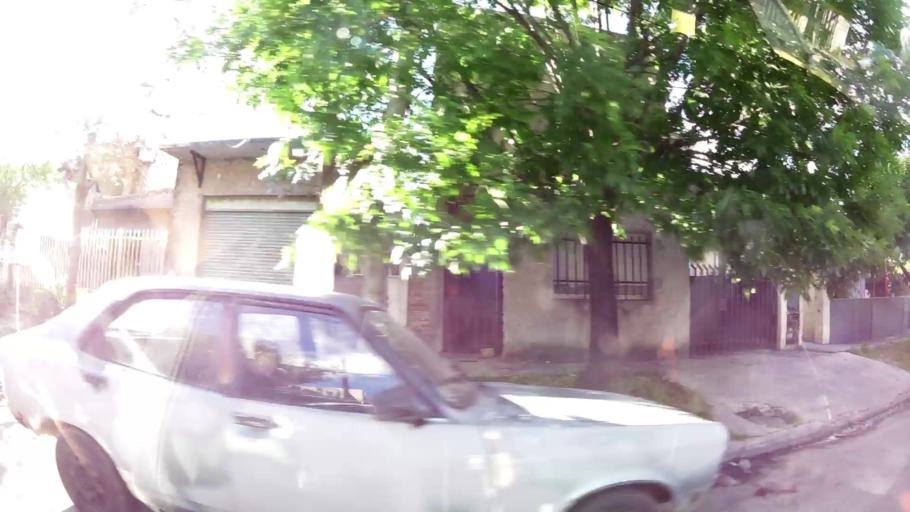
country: AR
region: Buenos Aires
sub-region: Partido de Moron
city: Moron
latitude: -34.6889
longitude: -58.6009
